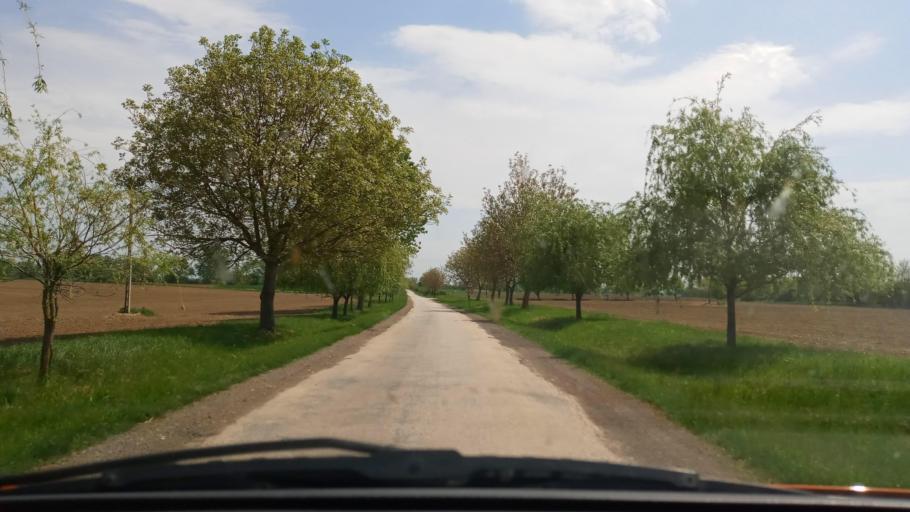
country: HU
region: Baranya
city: Villany
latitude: 45.8225
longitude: 18.5052
